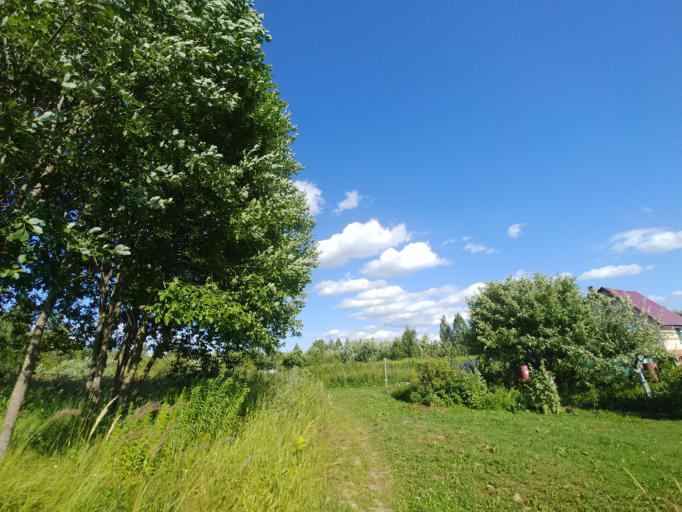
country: BY
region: Vitebsk
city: Vitebsk
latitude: 55.1198
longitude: 30.2903
